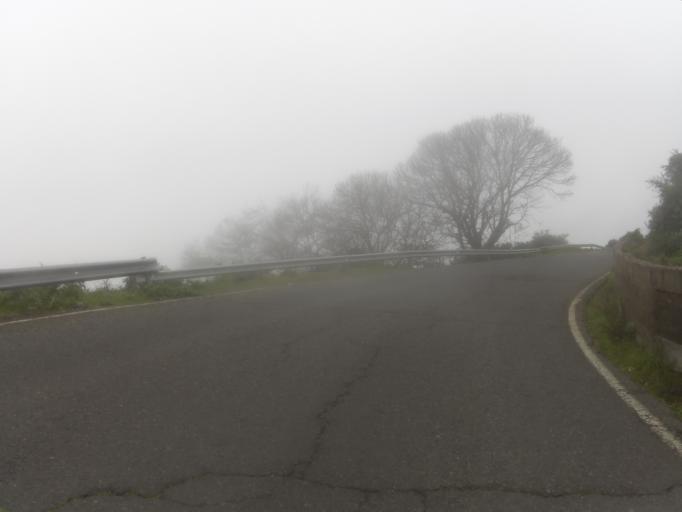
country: ES
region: Canary Islands
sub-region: Provincia de Las Palmas
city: Tejeda
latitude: 27.9847
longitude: -15.5733
